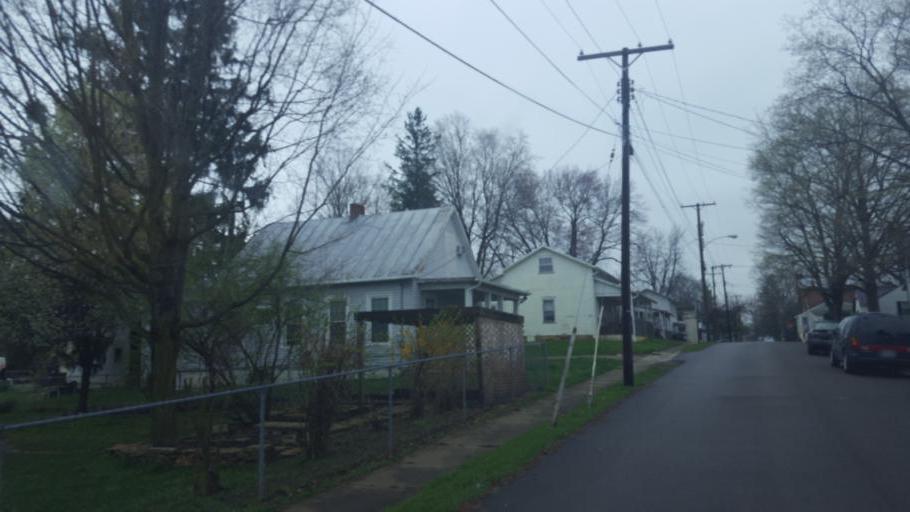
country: US
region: Ohio
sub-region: Morrow County
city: Mount Gilead
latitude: 40.5466
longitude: -82.8315
